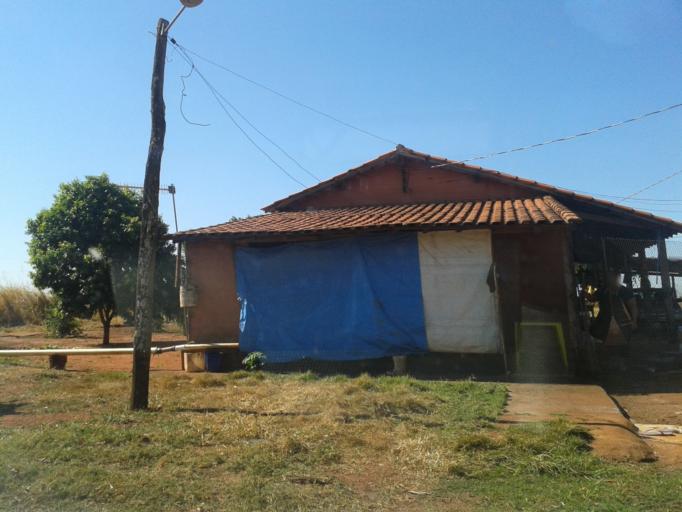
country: BR
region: Minas Gerais
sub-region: Santa Vitoria
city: Santa Vitoria
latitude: -19.0989
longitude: -50.3710
